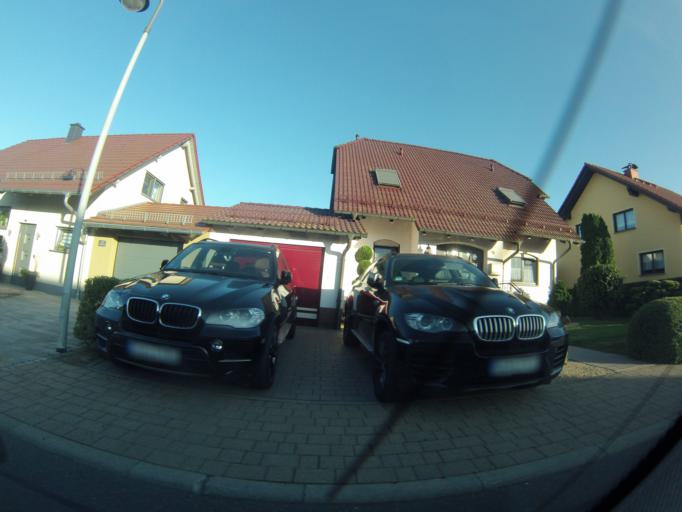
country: DE
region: Thuringia
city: Schmolln
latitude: 50.8906
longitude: 12.3712
